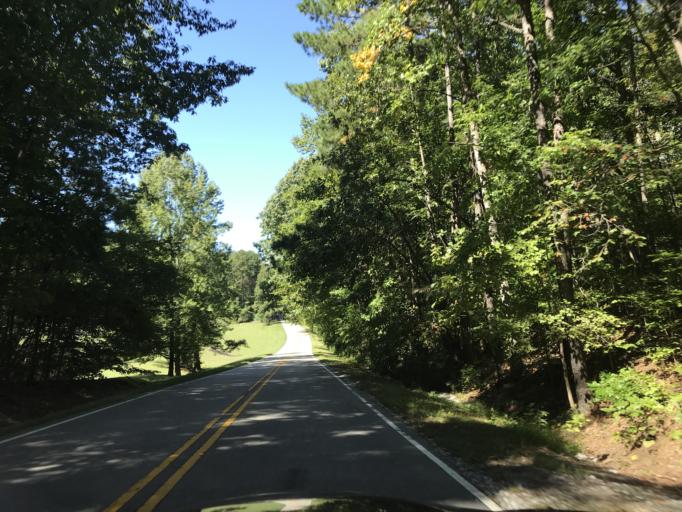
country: US
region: North Carolina
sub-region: Wake County
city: Wake Forest
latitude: 35.9494
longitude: -78.6065
